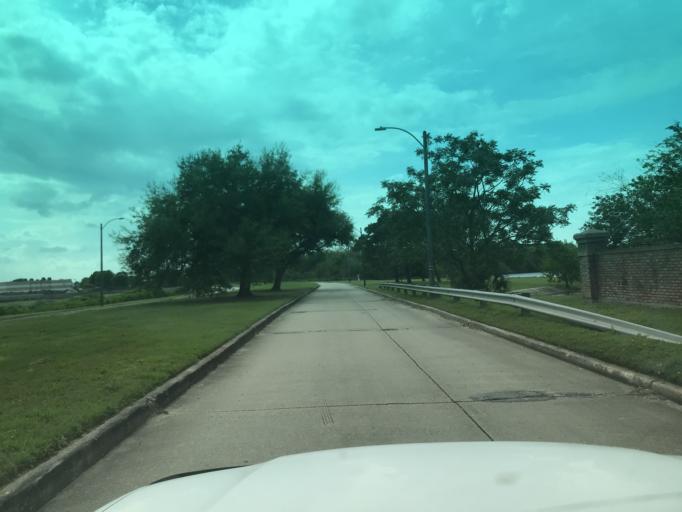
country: US
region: Louisiana
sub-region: Saint Bernard Parish
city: Chalmette
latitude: 30.0399
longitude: -89.9504
